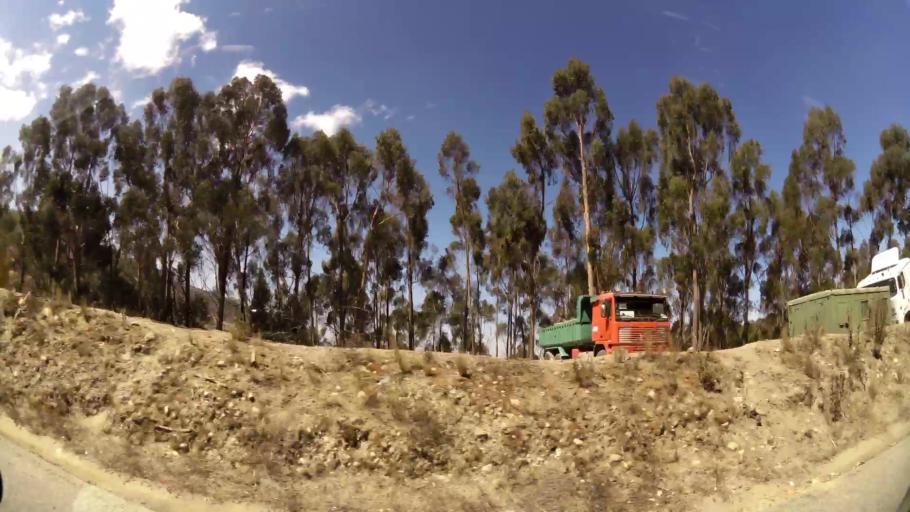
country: BO
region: La Paz
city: La Paz
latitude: -16.4700
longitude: -68.1566
